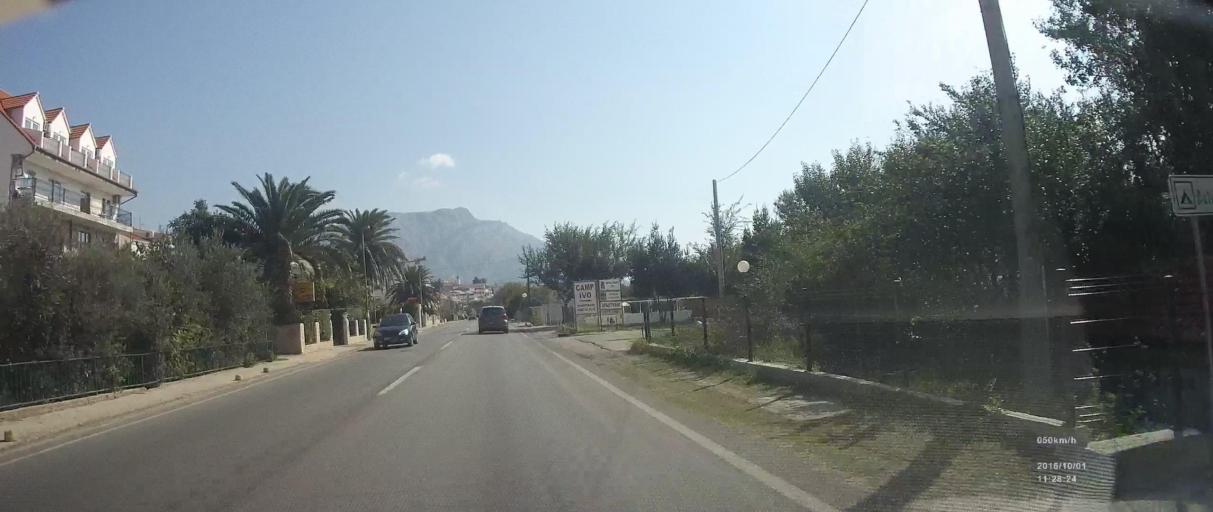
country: HR
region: Splitsko-Dalmatinska
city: Duce
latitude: 43.4412
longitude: 16.6576
